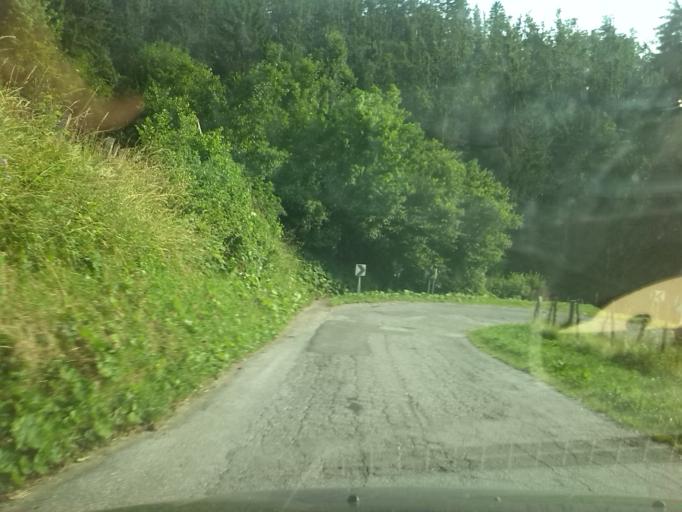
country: IT
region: Friuli Venezia Giulia
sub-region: Provincia di Udine
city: Cras
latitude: 46.2009
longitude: 13.6031
